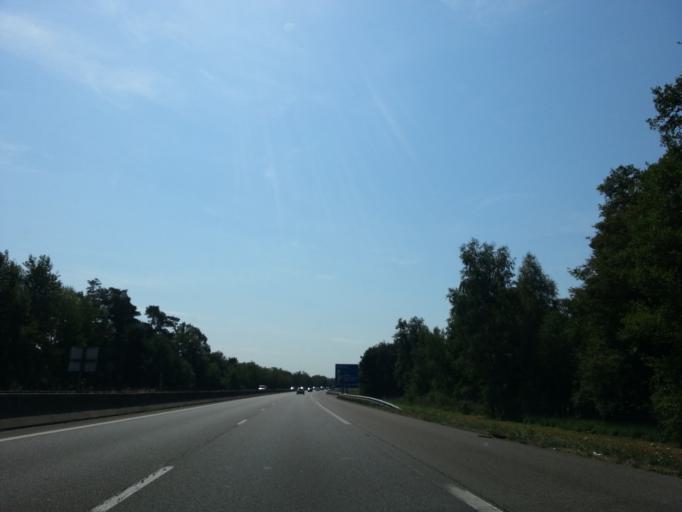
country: FR
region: Alsace
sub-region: Departement du Bas-Rhin
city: Vendenheim
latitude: 48.6955
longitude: 7.7230
